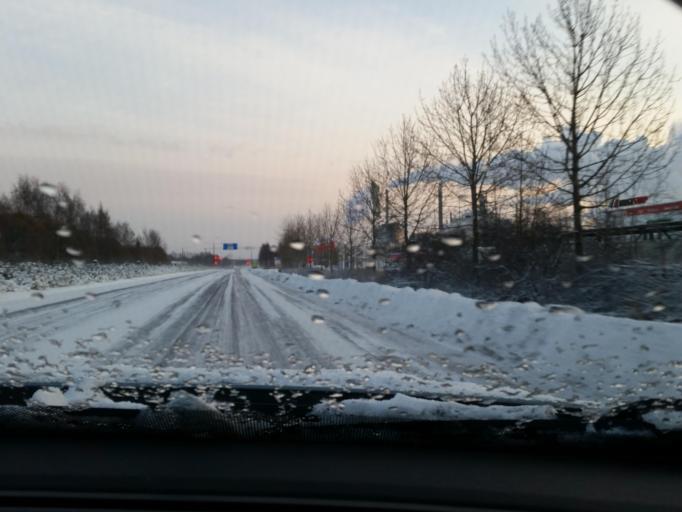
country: SE
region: Norrbotten
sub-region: Pitea Kommun
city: Pitea
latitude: 65.3200
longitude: 21.4298
